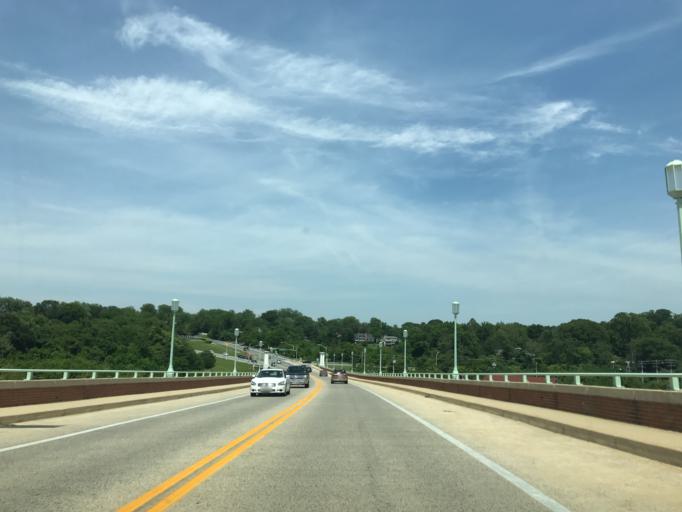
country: US
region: Maryland
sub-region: Anne Arundel County
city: Naval Academy
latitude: 38.9942
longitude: -76.4853
